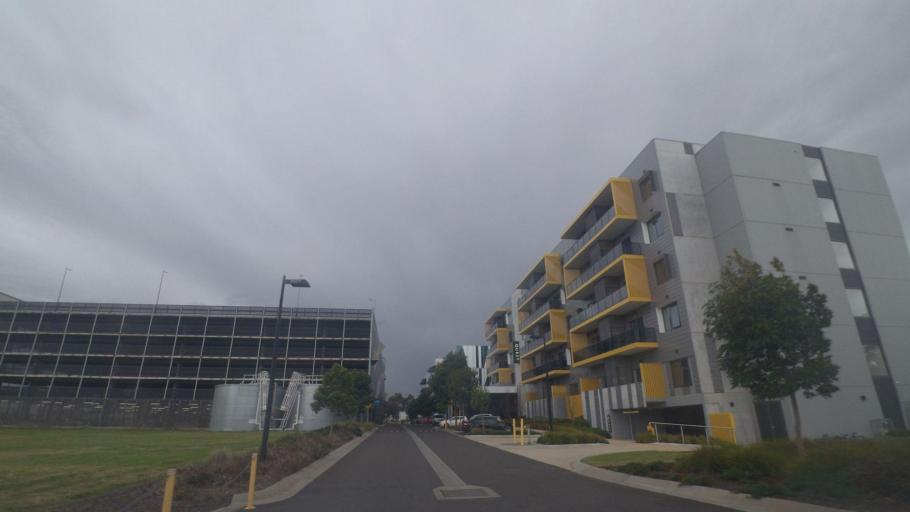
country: AU
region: Victoria
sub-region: Monash
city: Notting Hill
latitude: -37.9025
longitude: 145.1341
